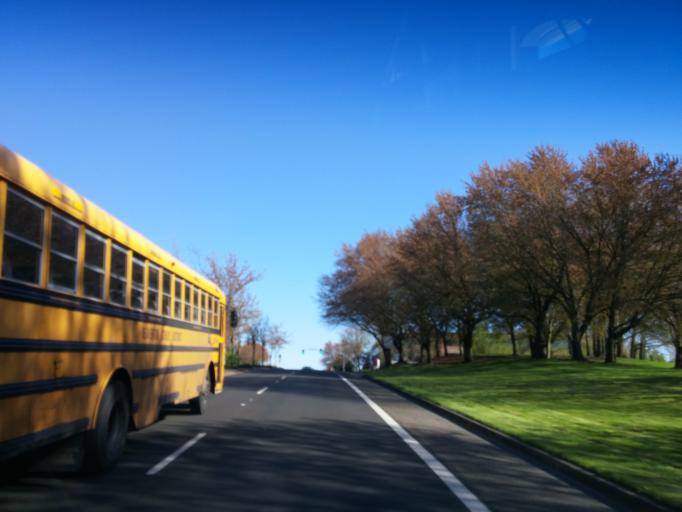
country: US
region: Oregon
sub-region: Washington County
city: Oak Hills
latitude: 45.5251
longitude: -122.8395
